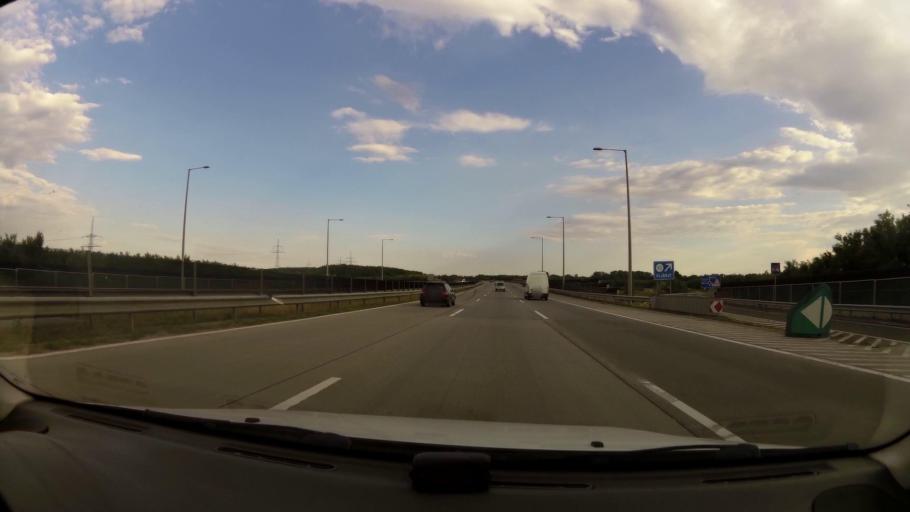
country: HU
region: Pest
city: Pecel
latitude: 47.4922
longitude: 19.3107
